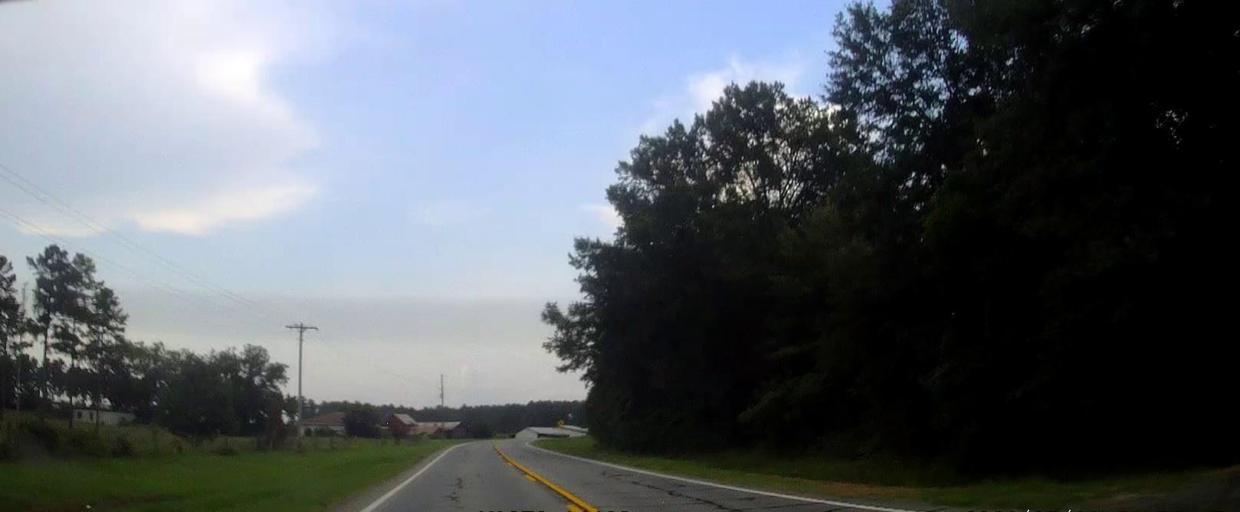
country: US
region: Georgia
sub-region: Laurens County
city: East Dublin
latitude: 32.5774
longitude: -82.8381
